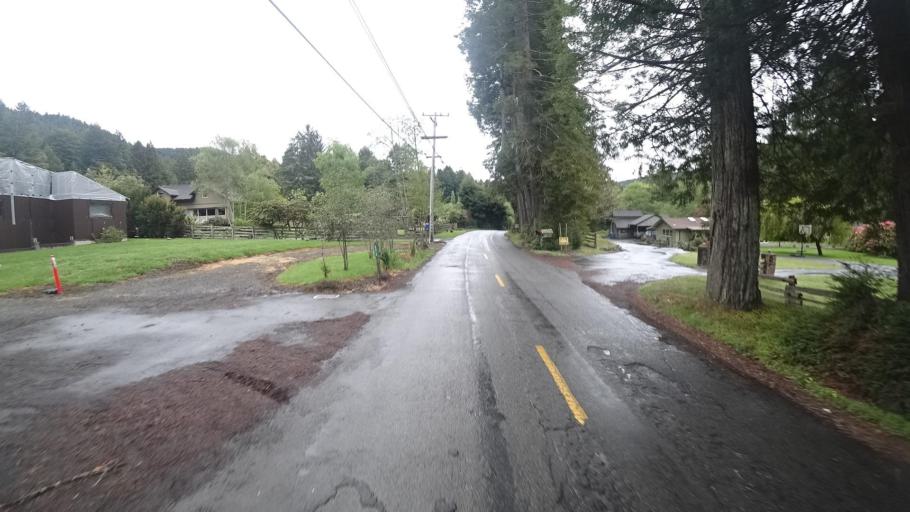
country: US
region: California
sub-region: Humboldt County
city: Bayside
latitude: 40.8308
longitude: -124.0405
